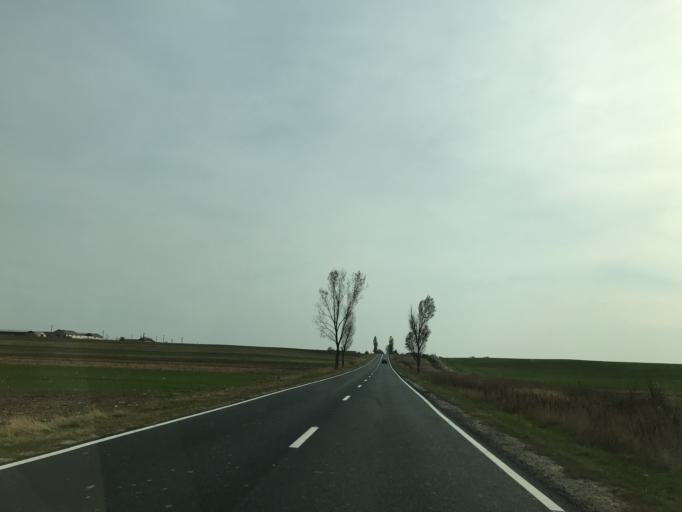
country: RO
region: Olt
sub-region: Comuna Brancoveni
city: Brancoveni
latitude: 44.3227
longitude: 24.2977
